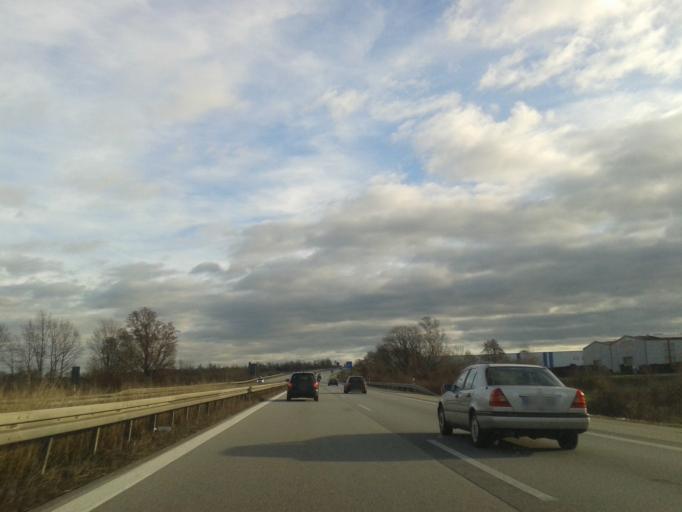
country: DE
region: Saxony
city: Goda
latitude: 51.1971
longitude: 14.3409
